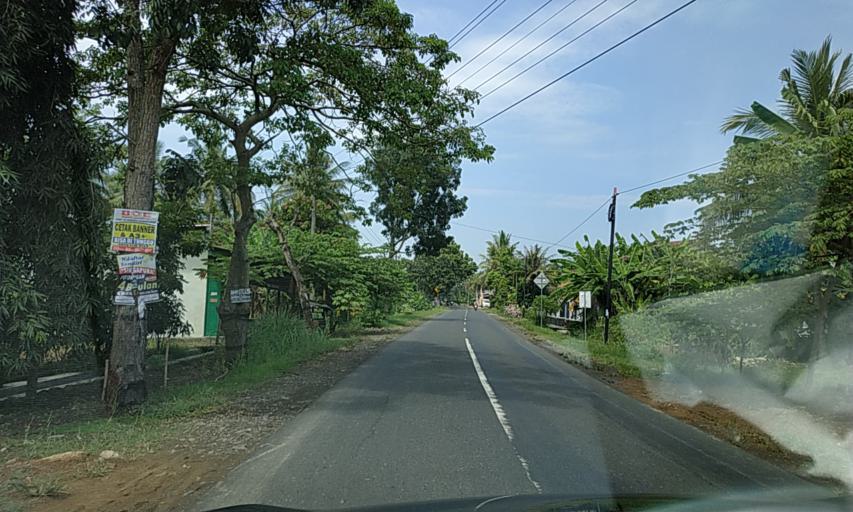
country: ID
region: Central Java
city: Mulyosari
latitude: -7.5165
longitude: 108.7842
